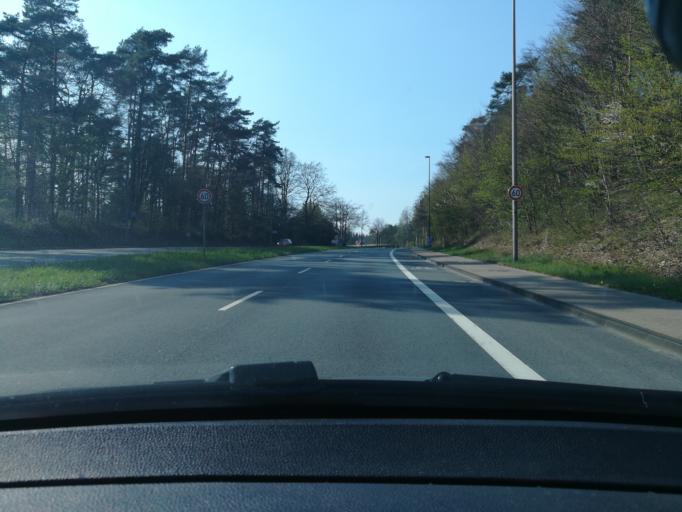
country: DE
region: North Rhine-Westphalia
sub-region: Regierungsbezirk Detmold
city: Bielefeld
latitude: 51.9793
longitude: 8.5334
